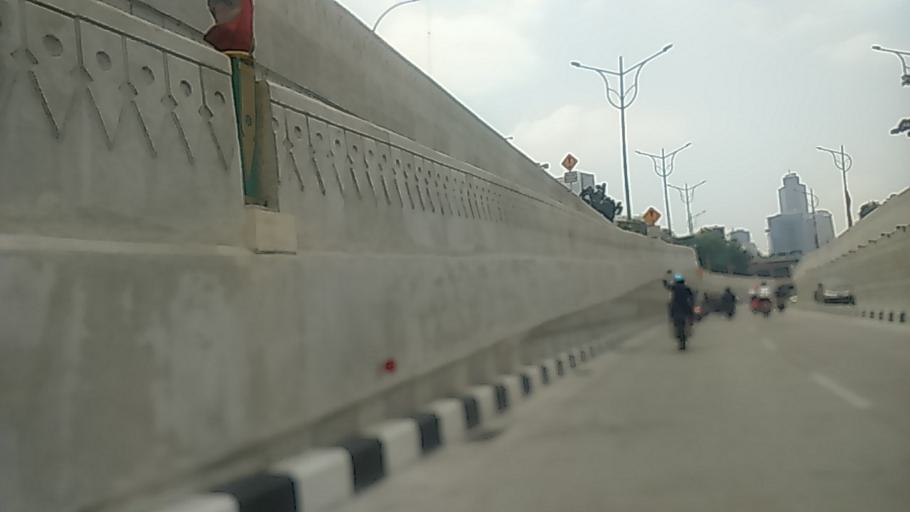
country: ID
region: Jakarta Raya
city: Jakarta
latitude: -6.2408
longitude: 106.8257
